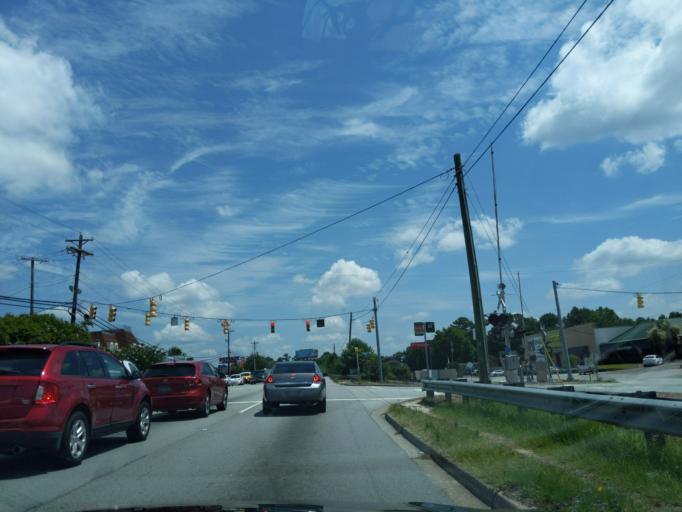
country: US
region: South Carolina
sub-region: Richland County
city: Dentsville
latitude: 34.0760
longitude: -80.9449
